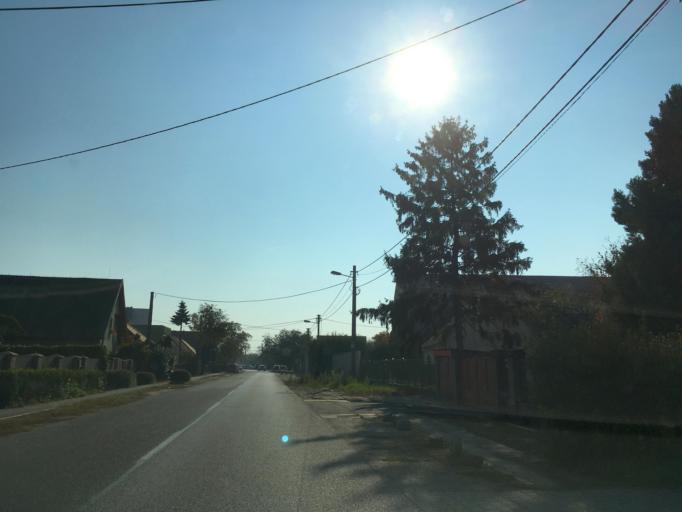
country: SK
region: Bratislavsky
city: Dunajska Luzna
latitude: 48.1335
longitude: 17.1956
